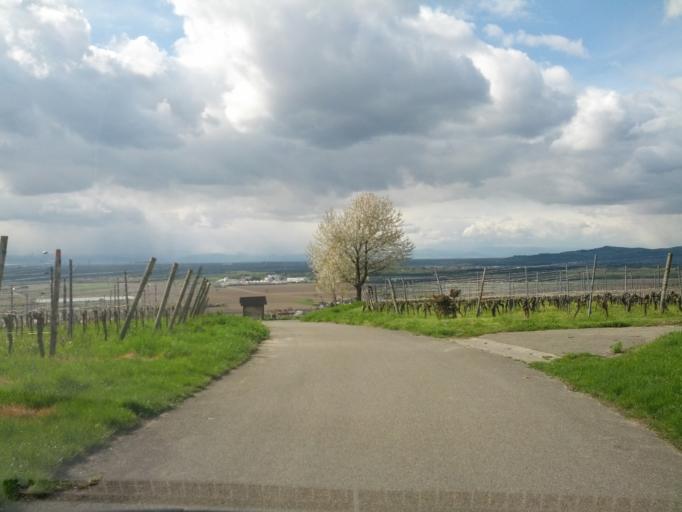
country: DE
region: Baden-Wuerttemberg
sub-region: Freiburg Region
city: Merdingen
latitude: 47.9764
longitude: 7.6795
